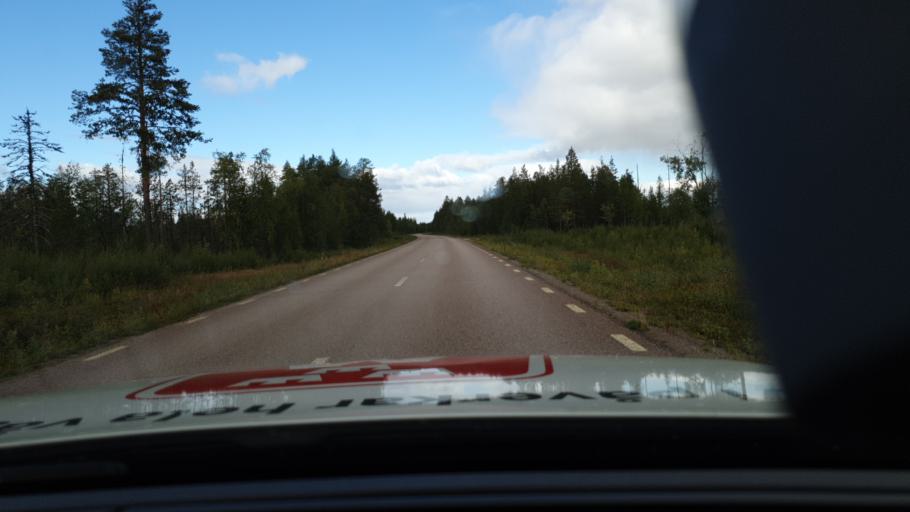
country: SE
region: Norrbotten
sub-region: Pajala Kommun
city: Pajala
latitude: 67.2275
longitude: 22.7853
